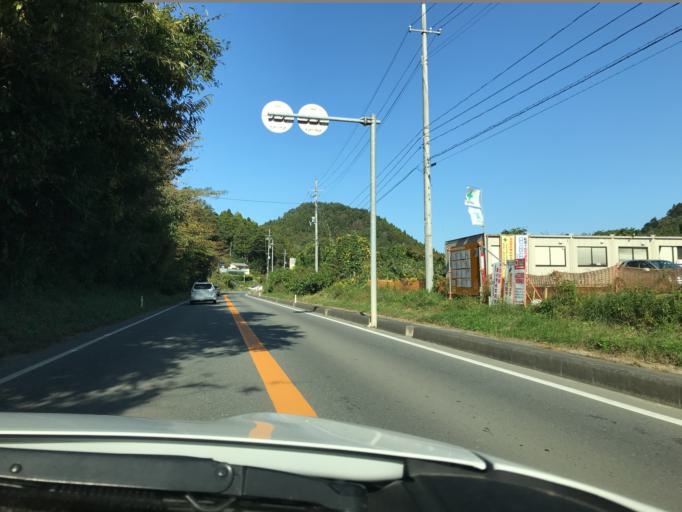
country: JP
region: Miyagi
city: Marumori
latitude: 37.7712
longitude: 140.8615
